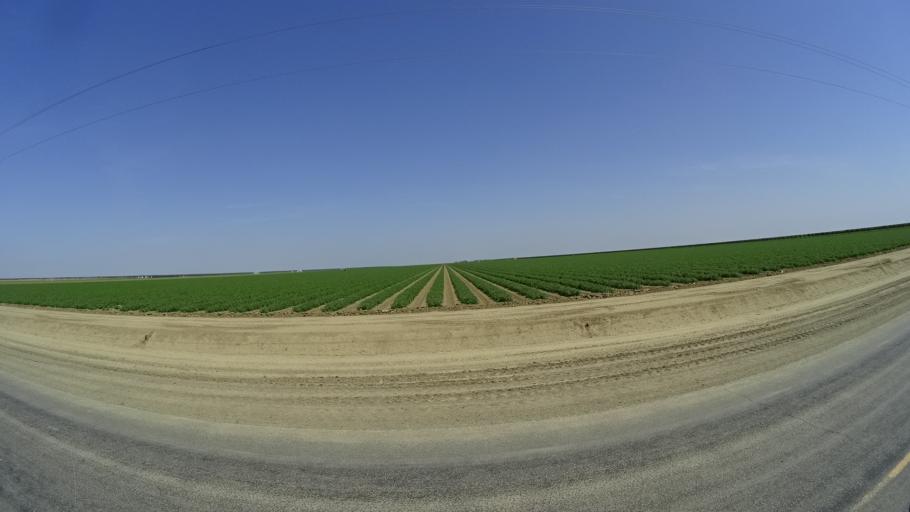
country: US
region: California
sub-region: Kings County
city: Kettleman City
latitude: 36.1377
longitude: -119.9621
